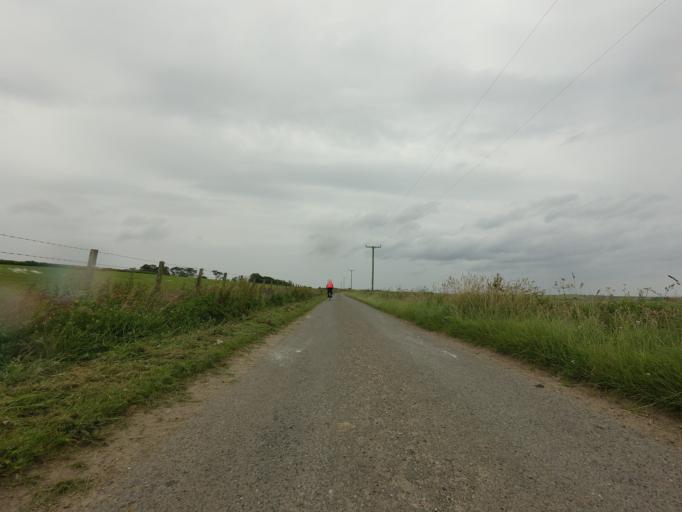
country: GB
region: Scotland
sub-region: Moray
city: Cullen
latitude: 57.6679
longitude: -2.7662
